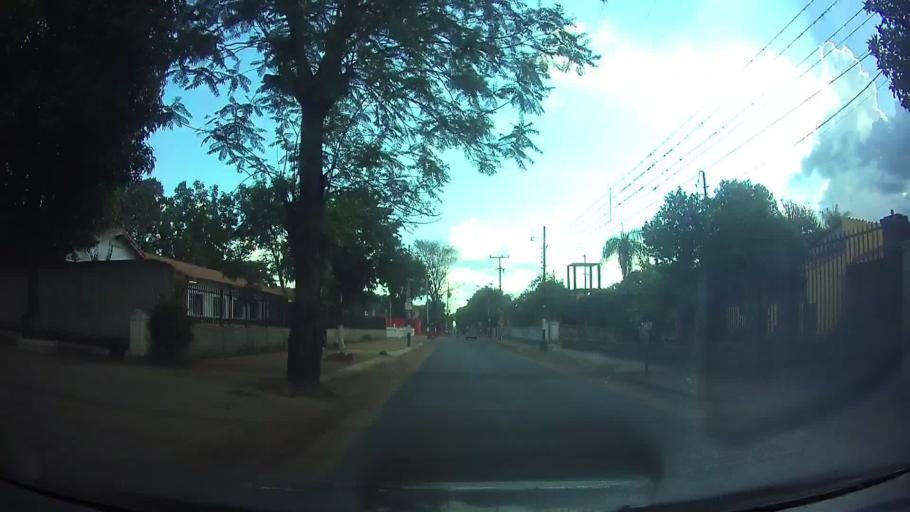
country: PY
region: Central
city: Aregua
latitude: -25.2866
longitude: -57.4385
